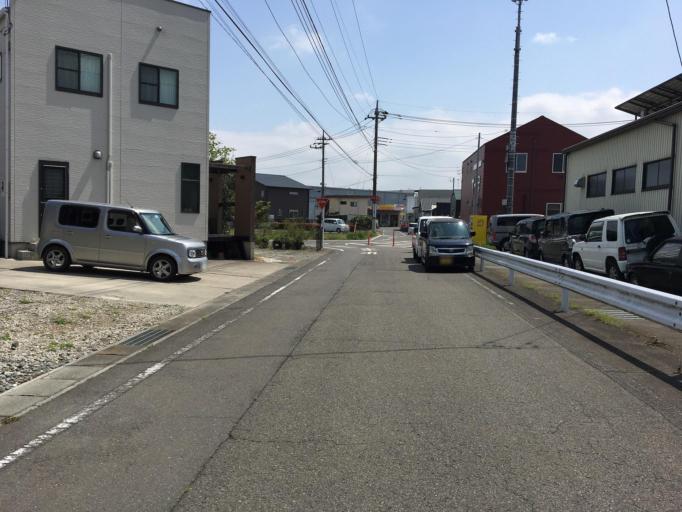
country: JP
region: Gunma
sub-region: Sawa-gun
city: Tamamura
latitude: 36.2987
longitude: 139.1349
